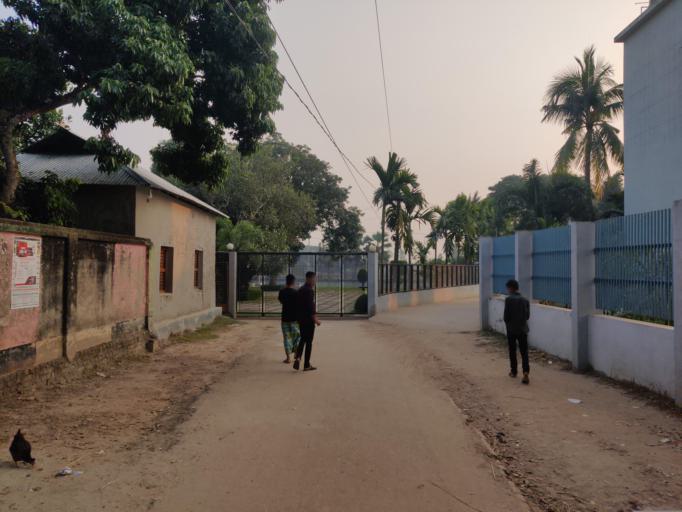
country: BD
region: Dhaka
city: Bajitpur
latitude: 24.1556
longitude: 90.7637
